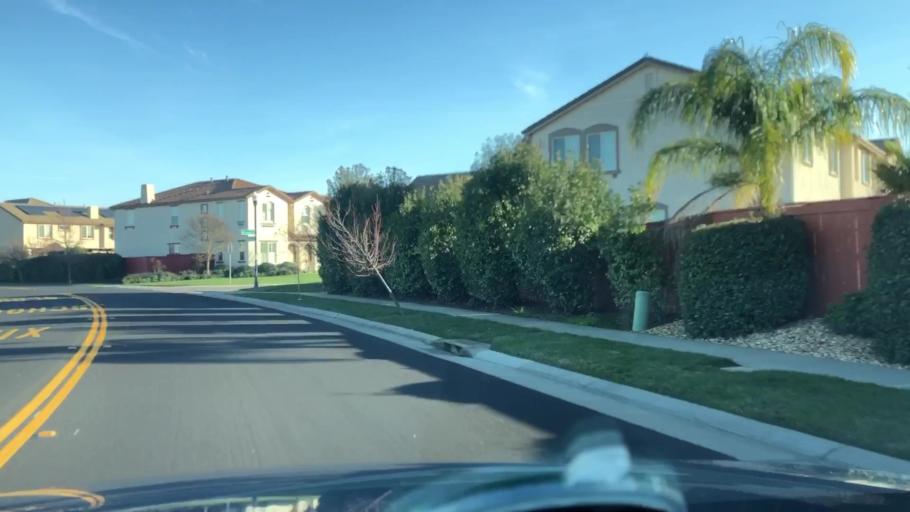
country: US
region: California
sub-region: Sacramento County
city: Laguna
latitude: 38.3988
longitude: -121.4076
